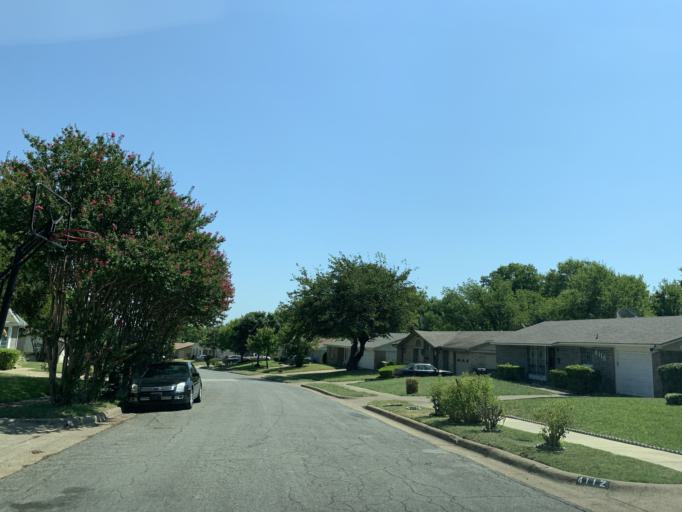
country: US
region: Texas
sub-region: Dallas County
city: Hutchins
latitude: 32.6749
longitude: -96.7514
